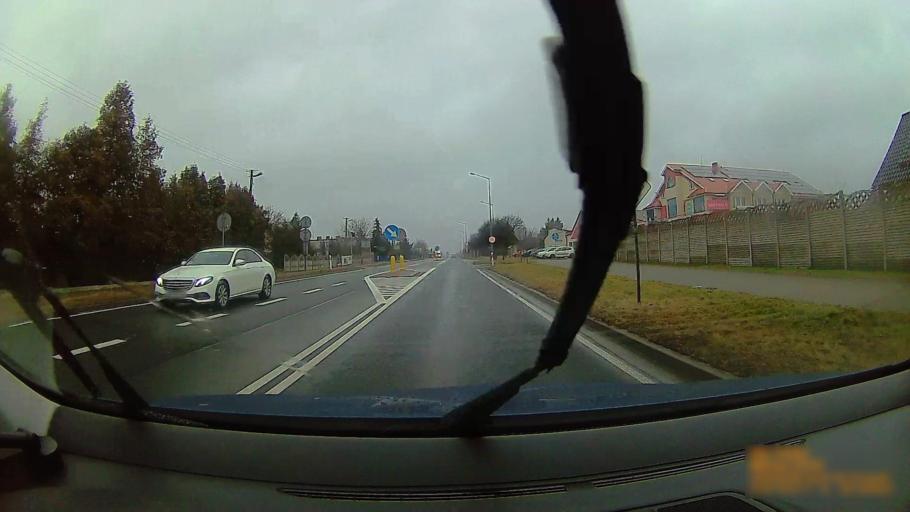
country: PL
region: Greater Poland Voivodeship
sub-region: Konin
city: Konin
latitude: 52.1767
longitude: 18.2715
